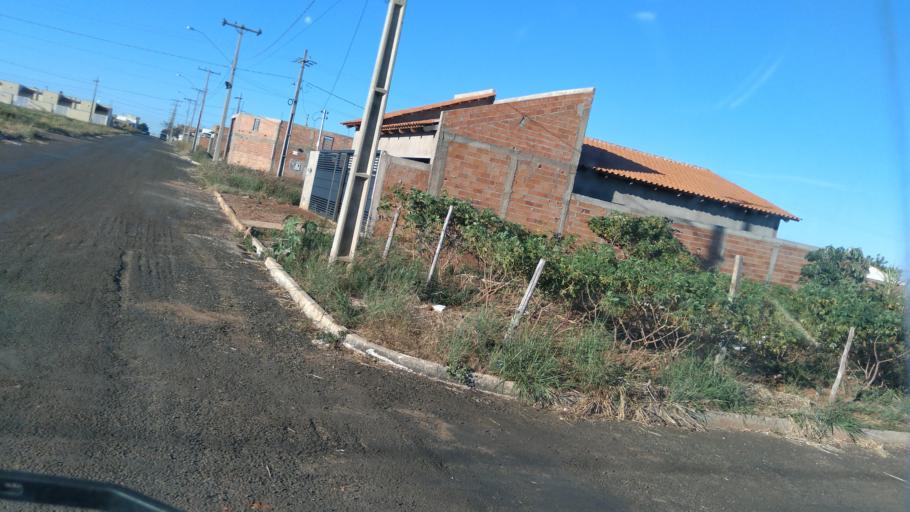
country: BR
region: Goias
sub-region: Mineiros
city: Mineiros
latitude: -17.5420
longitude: -52.5549
